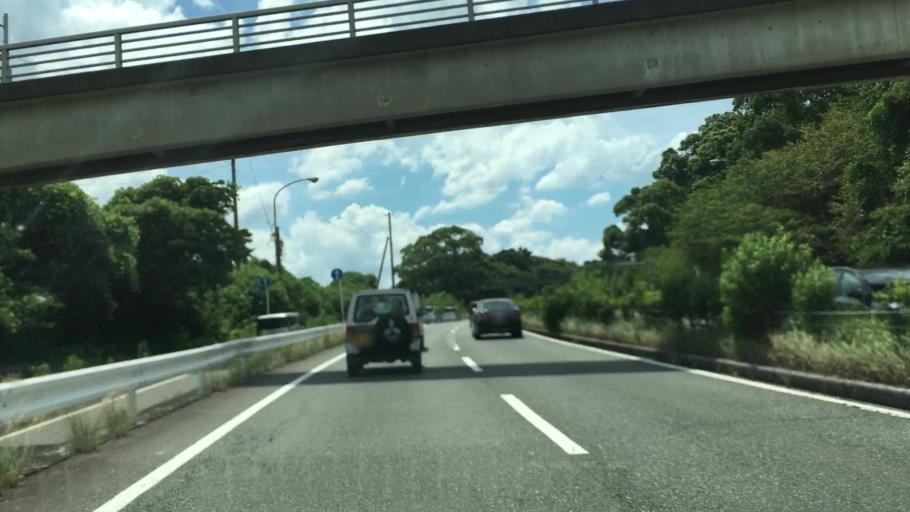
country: JP
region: Saga Prefecture
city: Tosu
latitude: 33.4018
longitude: 130.5126
